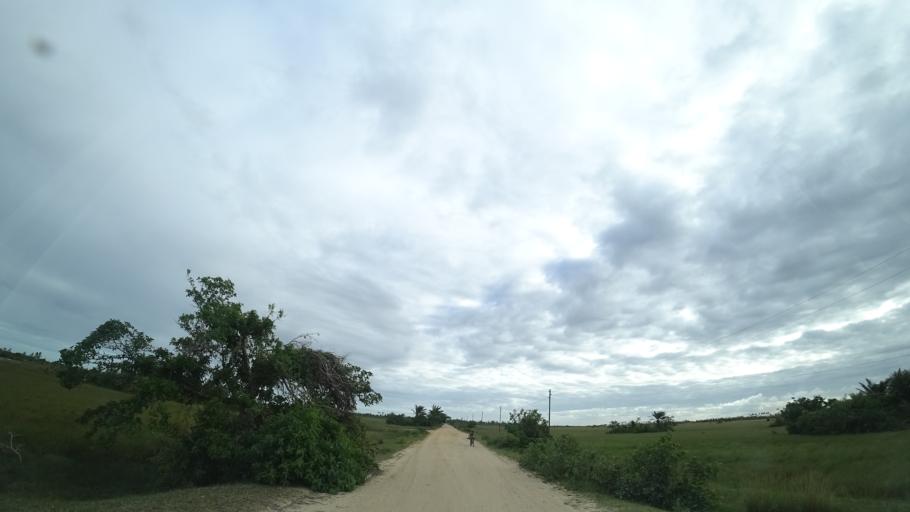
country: MZ
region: Sofala
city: Beira
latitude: -19.7308
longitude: 34.9806
